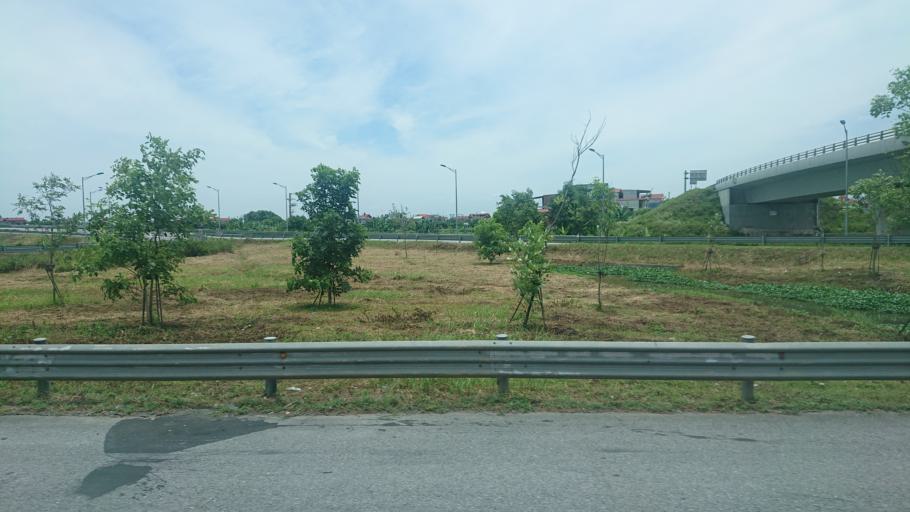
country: VN
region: Hai Phong
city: An Lao
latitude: 20.8027
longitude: 106.5268
